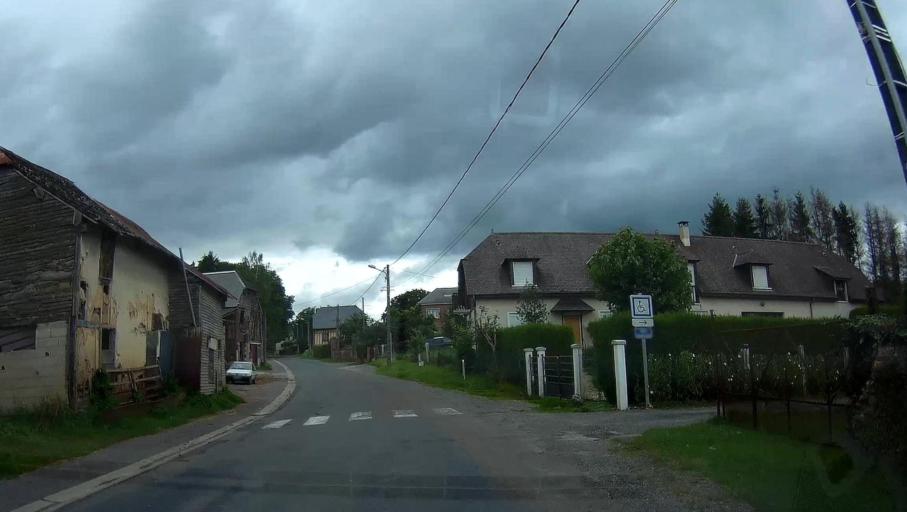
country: FR
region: Picardie
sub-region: Departement de l'Aisne
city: Rozoy-sur-Serre
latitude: 49.6911
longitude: 4.2466
